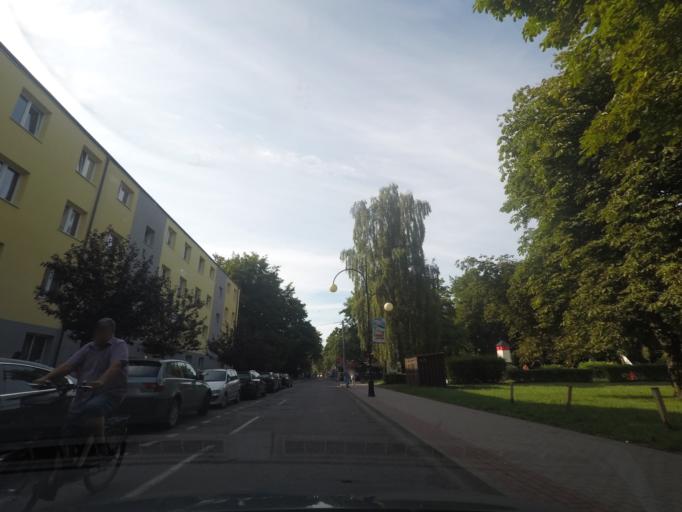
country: PL
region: Pomeranian Voivodeship
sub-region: Powiat leborski
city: Leba
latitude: 54.7618
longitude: 17.5531
